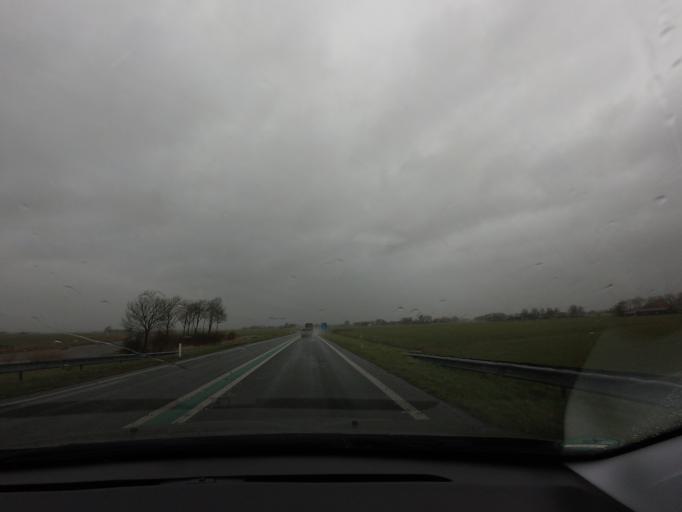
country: NL
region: Friesland
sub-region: Sudwest Fryslan
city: Bolsward
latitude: 53.0881
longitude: 5.5273
